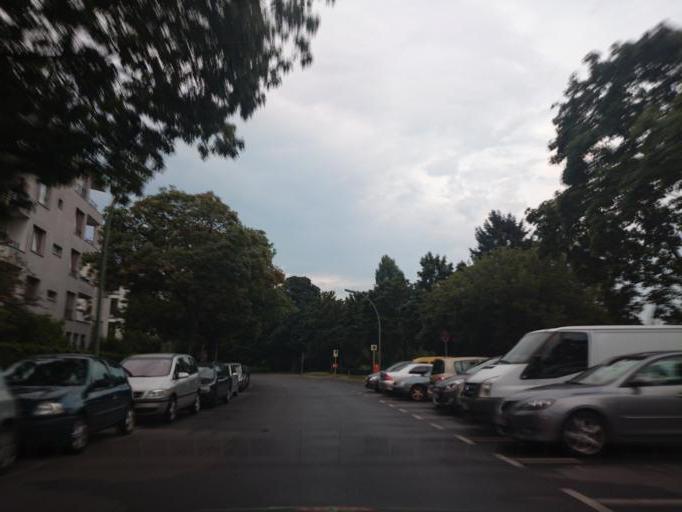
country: DE
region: Berlin
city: Baumschulenweg
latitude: 52.4607
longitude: 13.4738
